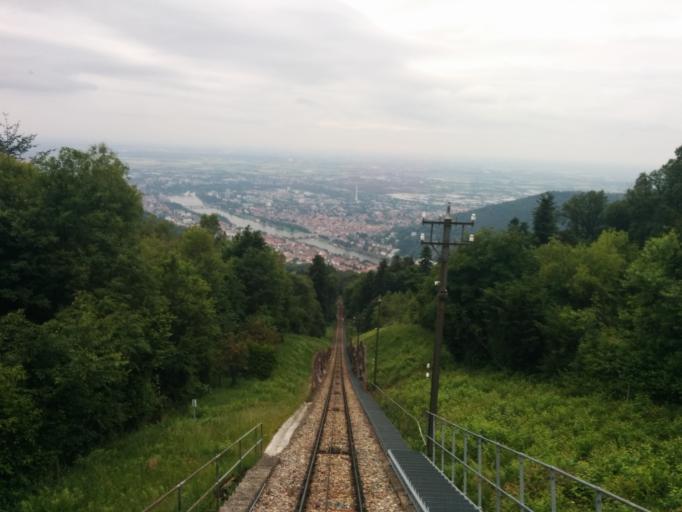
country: DE
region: Baden-Wuerttemberg
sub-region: Karlsruhe Region
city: Heidelberg
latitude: 49.4036
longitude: 8.7267
